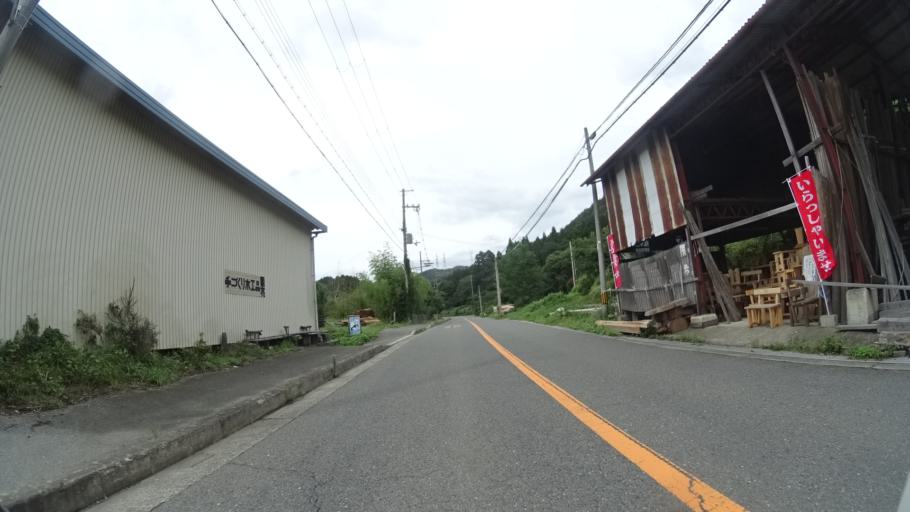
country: JP
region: Kyoto
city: Kameoka
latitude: 34.9798
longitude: 135.4692
